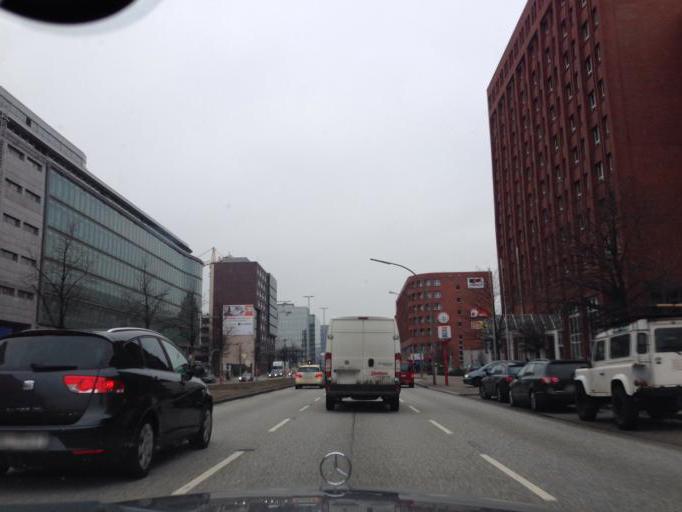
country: DE
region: Hamburg
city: Hammerbrook
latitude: 53.5442
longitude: 10.0315
